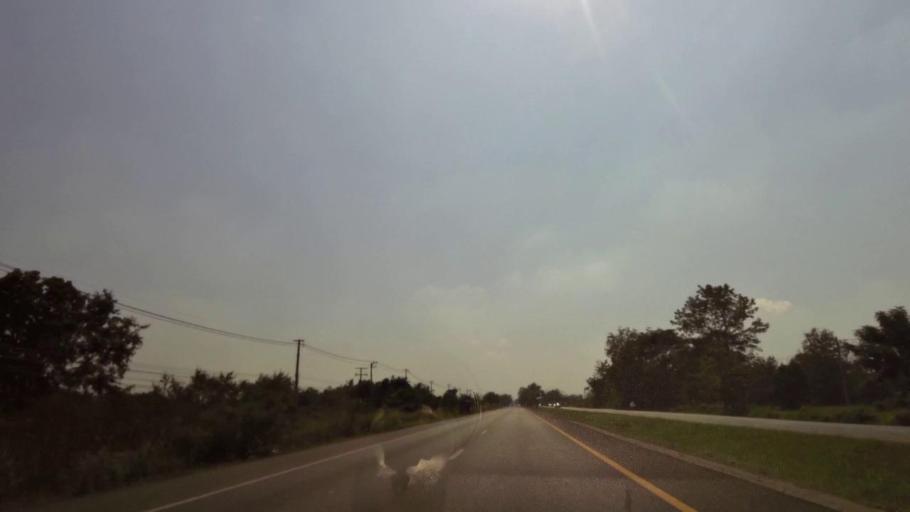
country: TH
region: Phichit
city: Bueng Na Rang
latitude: 16.2603
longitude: 100.1263
